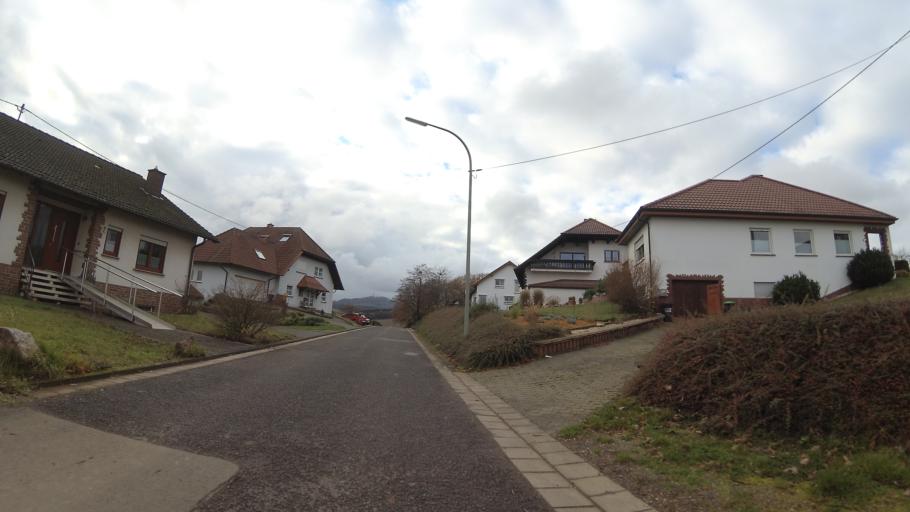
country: DE
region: Saarland
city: Oberthal
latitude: 49.5109
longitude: 7.0680
